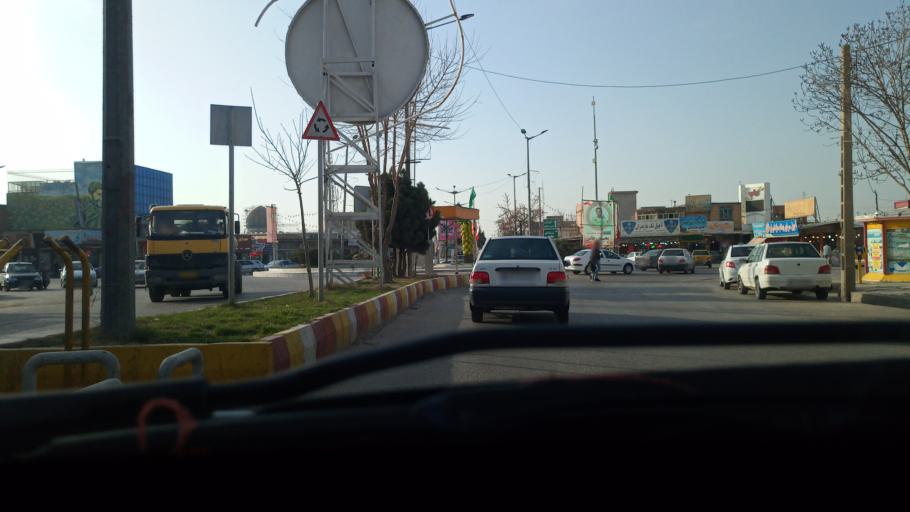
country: IR
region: Khorasan-e Shomali
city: Faruj
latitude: 37.2319
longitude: 58.2198
